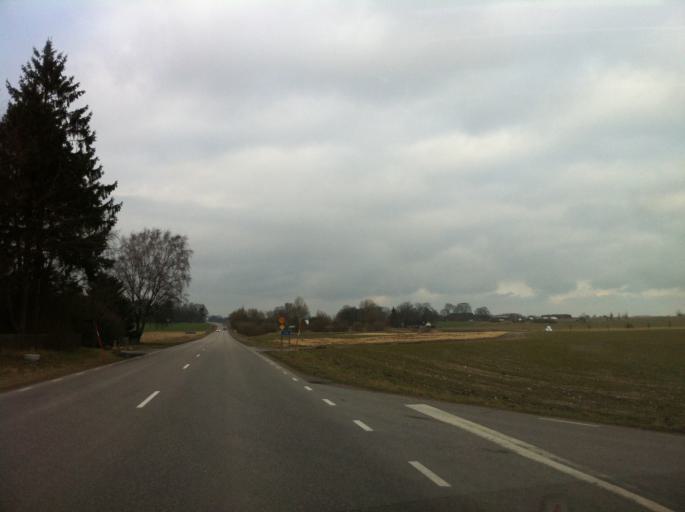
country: SE
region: Skane
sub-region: Kavlinge Kommun
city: Kaevlinge
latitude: 55.8213
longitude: 13.0818
